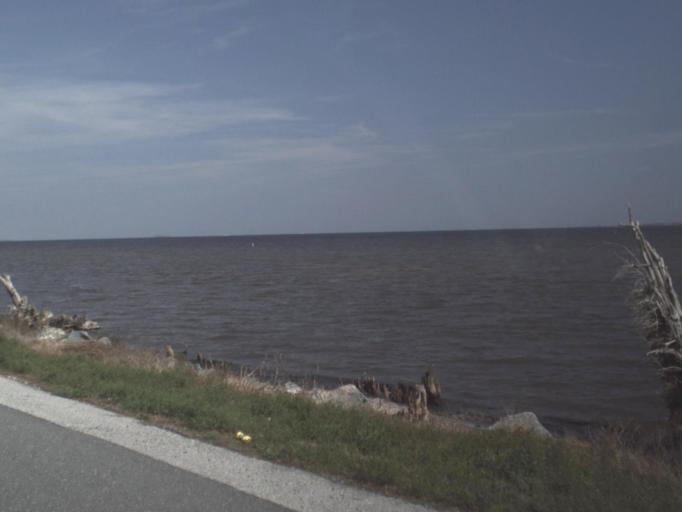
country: US
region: Florida
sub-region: Franklin County
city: Eastpoint
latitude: 29.7619
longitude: -84.8167
